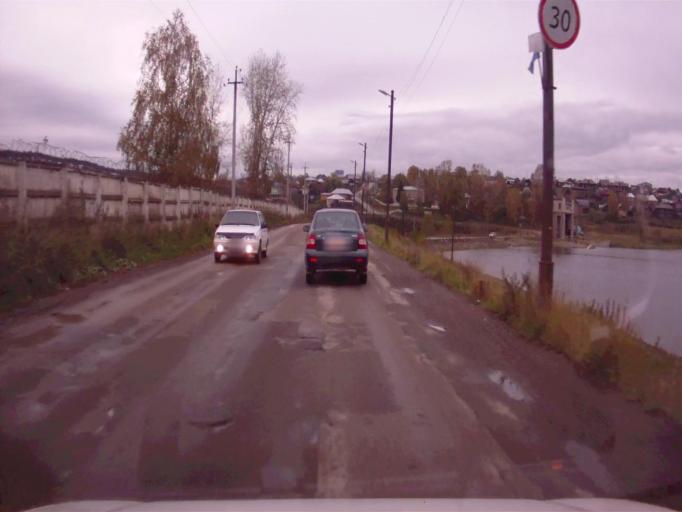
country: RU
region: Chelyabinsk
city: Nyazepetrovsk
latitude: 56.0548
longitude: 59.5927
